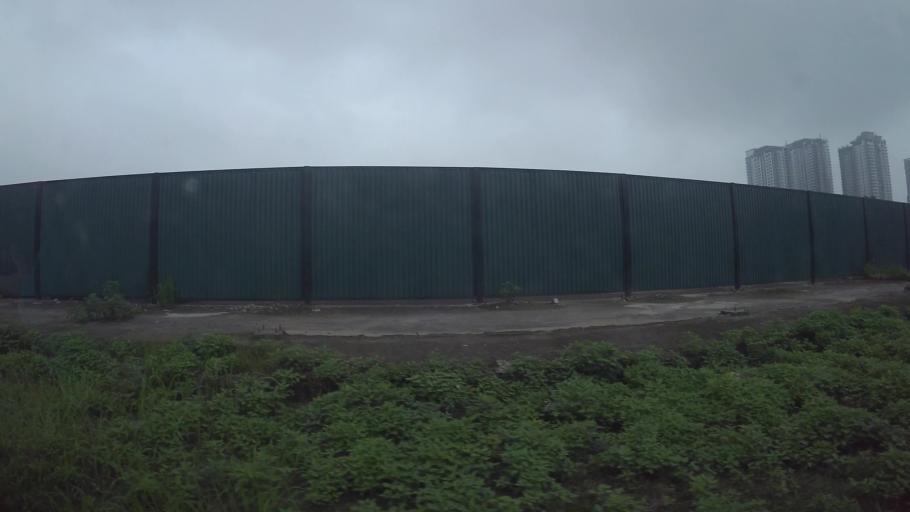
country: VN
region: Ha Noi
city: Van Dien
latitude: 20.9762
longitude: 105.8786
